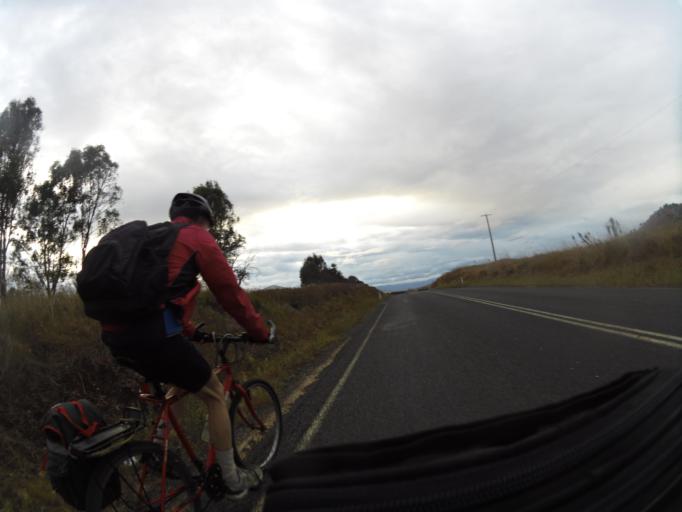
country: AU
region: New South Wales
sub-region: Greater Hume Shire
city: Holbrook
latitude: -36.0516
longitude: 147.9340
